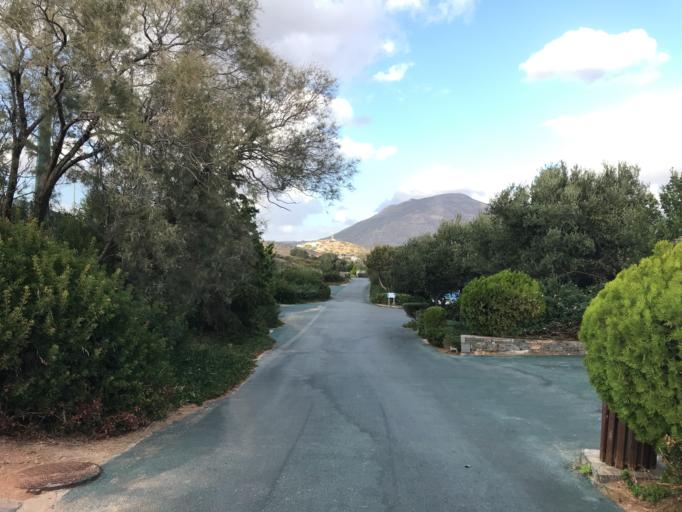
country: GR
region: Attica
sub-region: Nomarchia Anatolikis Attikis
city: Saronida
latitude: 37.7748
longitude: 23.8873
